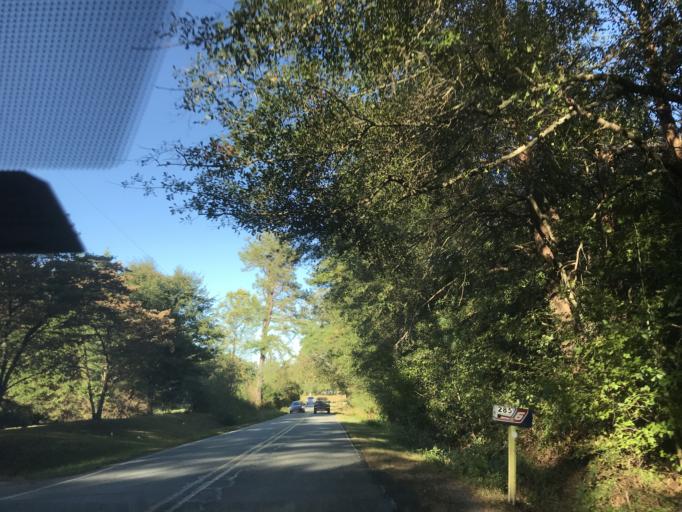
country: US
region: South Carolina
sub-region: Spartanburg County
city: Mayo
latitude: 35.0994
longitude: -81.8498
